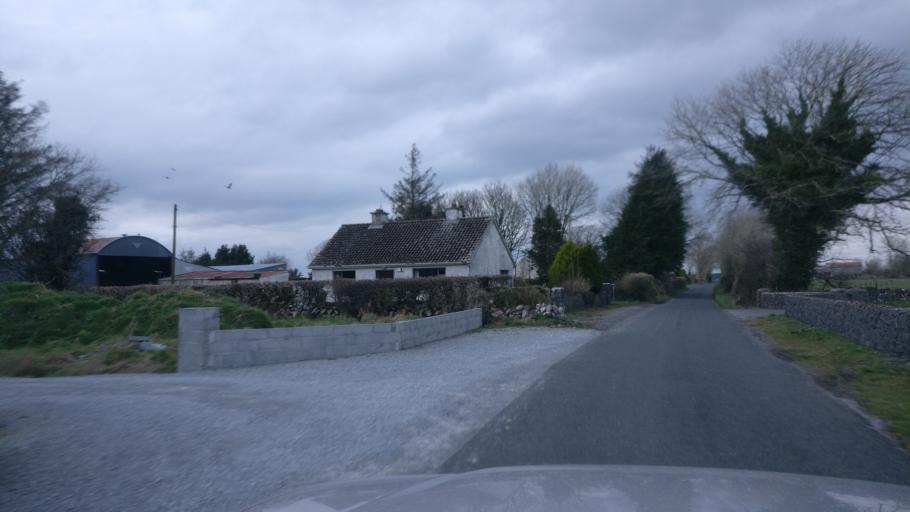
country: IE
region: Connaught
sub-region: County Galway
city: Loughrea
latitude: 53.2510
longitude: -8.5125
